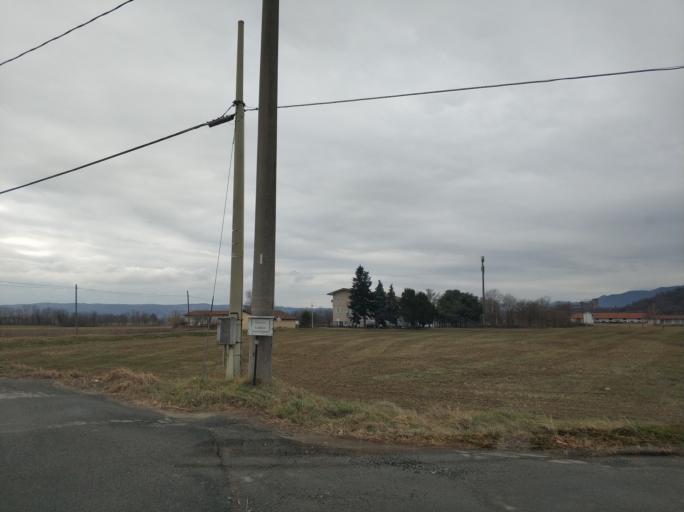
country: IT
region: Piedmont
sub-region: Provincia di Torino
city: Pavone Canavese
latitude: 45.4376
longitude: 7.8760
